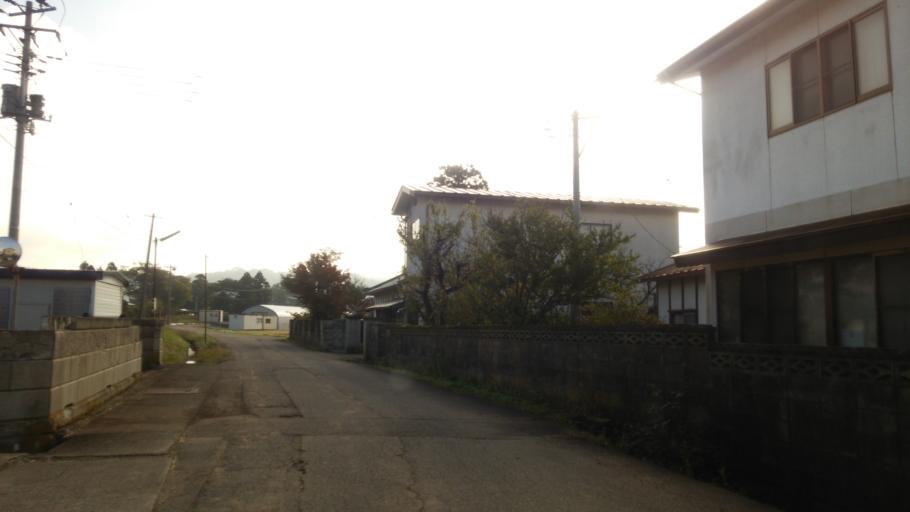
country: JP
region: Fukushima
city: Kitakata
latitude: 37.5421
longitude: 139.9356
